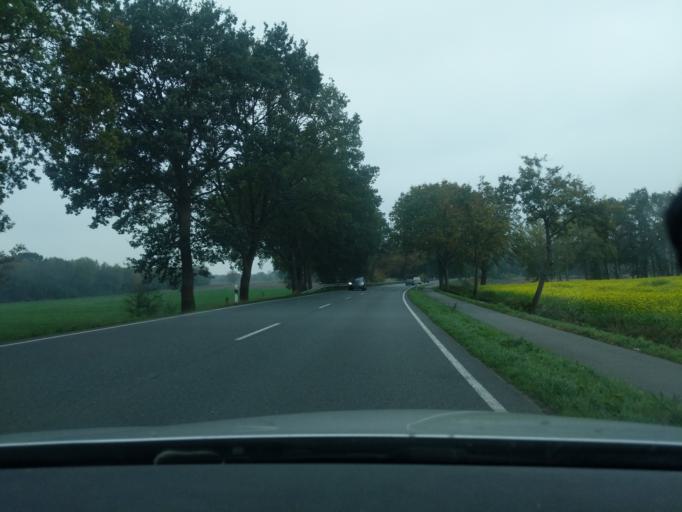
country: DE
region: Lower Saxony
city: Heinbockel
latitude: 53.5968
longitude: 9.3263
